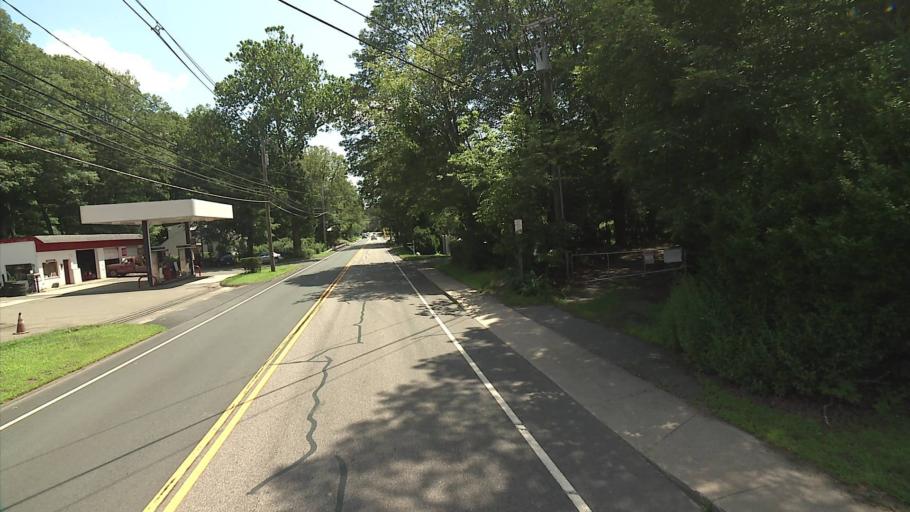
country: US
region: Connecticut
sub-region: Middlesex County
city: Deep River Center
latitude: 41.3728
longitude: -72.4298
